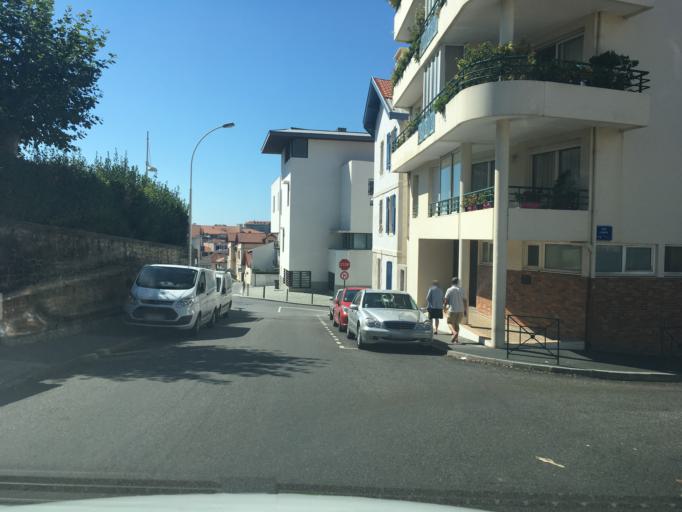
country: FR
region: Aquitaine
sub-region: Departement des Pyrenees-Atlantiques
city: Biarritz
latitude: 43.4807
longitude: -1.5530
